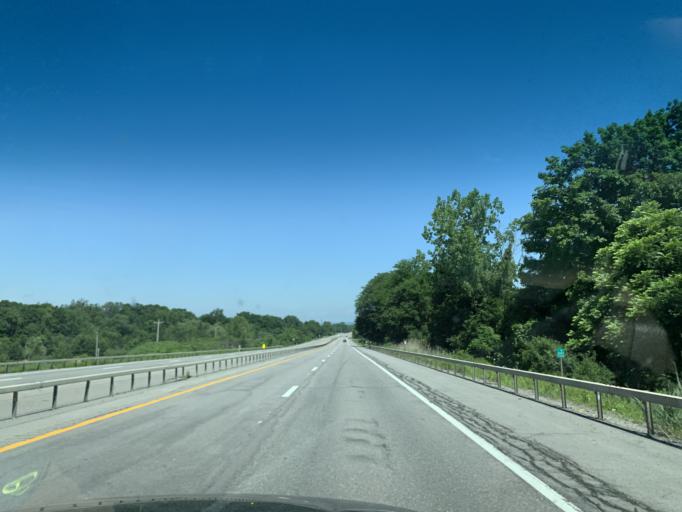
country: US
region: New York
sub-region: Oneida County
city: Washington Mills
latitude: 43.0440
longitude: -75.2740
